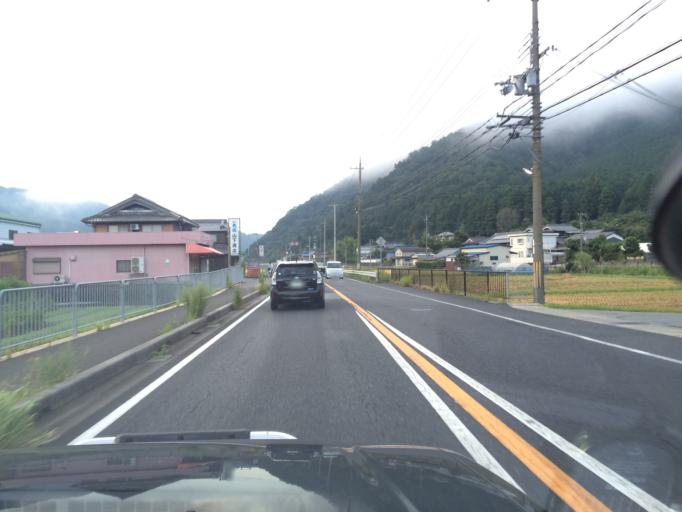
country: JP
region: Hyogo
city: Nishiwaki
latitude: 35.1219
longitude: 135.0065
